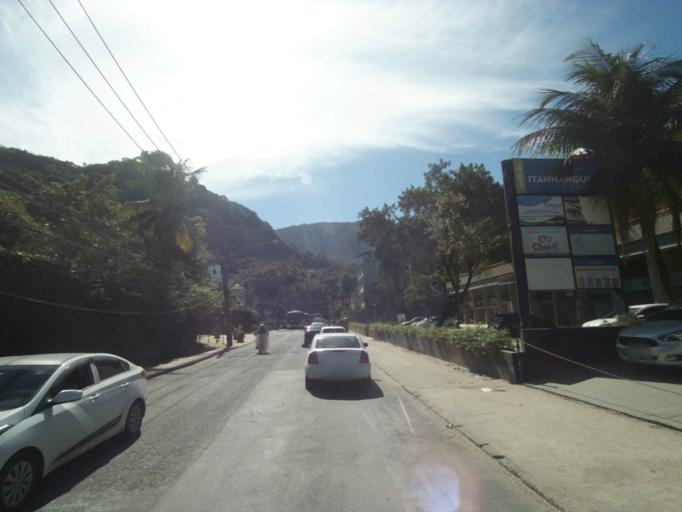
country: BR
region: Rio de Janeiro
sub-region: Rio De Janeiro
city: Rio de Janeiro
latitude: -22.9894
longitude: -43.3113
